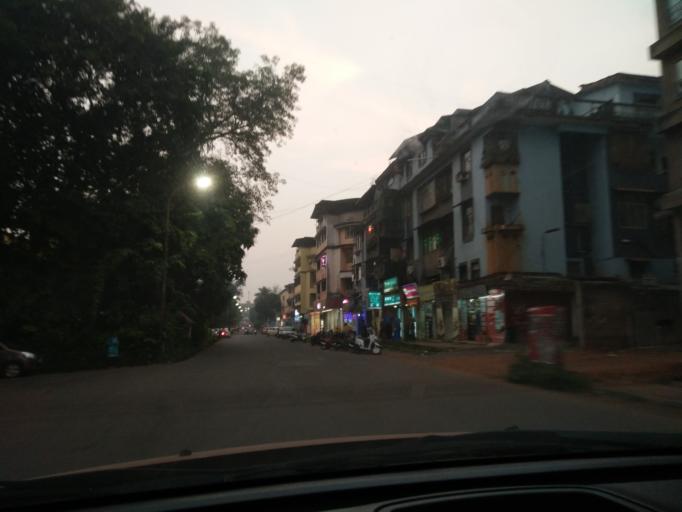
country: IN
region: Goa
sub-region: South Goa
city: Davorlim
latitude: 15.2809
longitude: 73.9780
